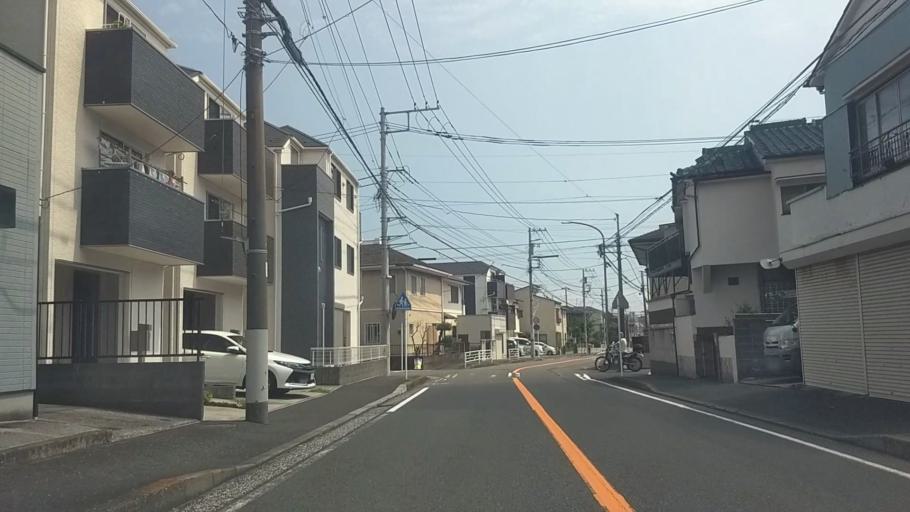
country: JP
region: Kanagawa
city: Yokohama
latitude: 35.4927
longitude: 139.6405
